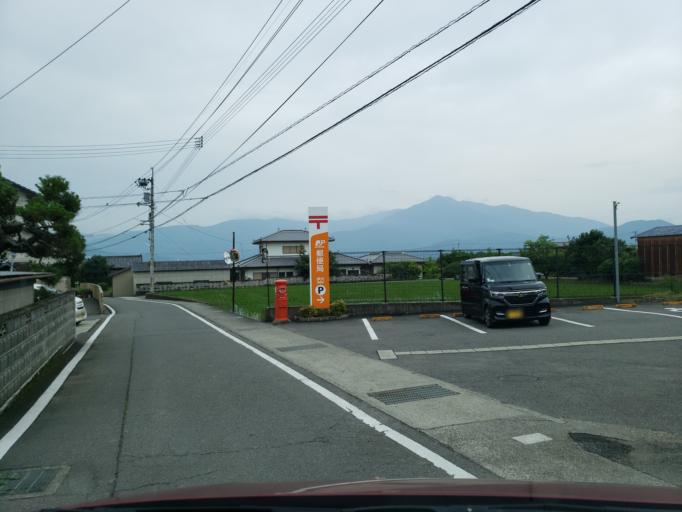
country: JP
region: Tokushima
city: Wakimachi
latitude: 34.0924
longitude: 134.2290
